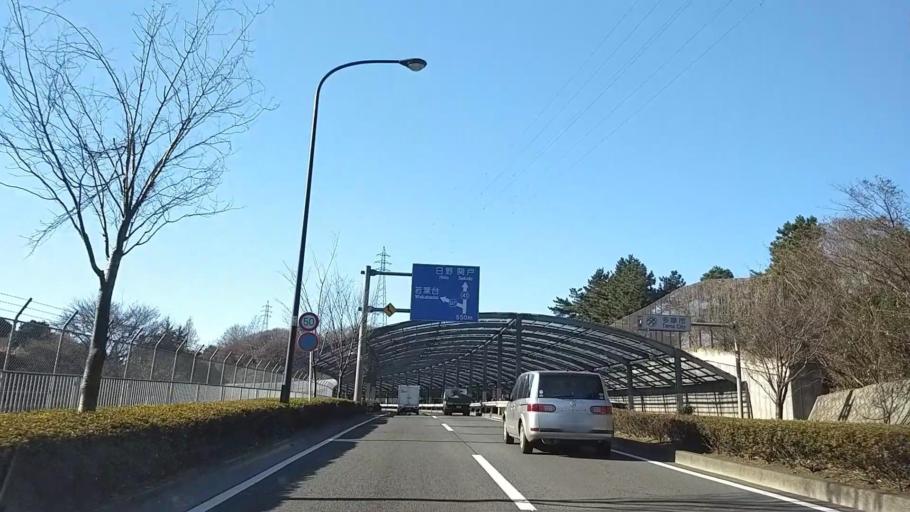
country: JP
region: Tokyo
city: Kokubunji
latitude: 35.6443
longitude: 139.4694
